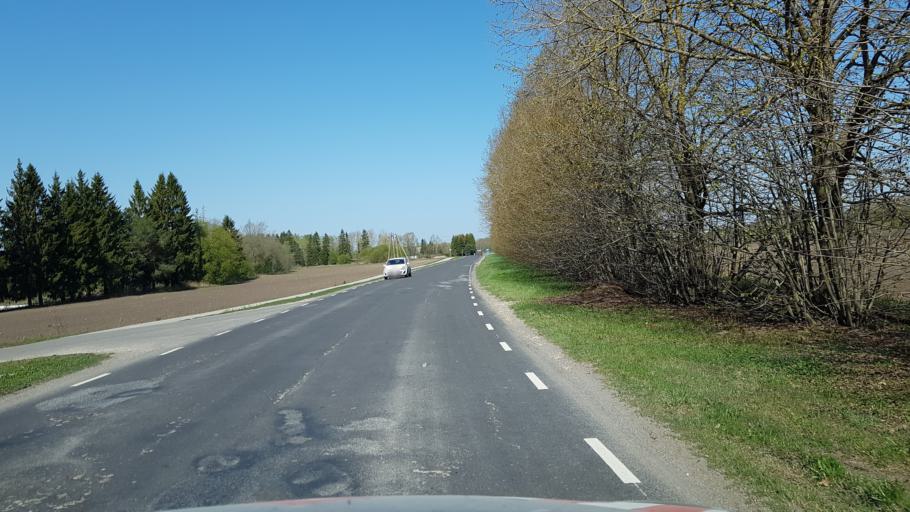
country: EE
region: Harju
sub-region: Joelaehtme vald
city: Loo
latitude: 59.4185
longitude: 24.9431
